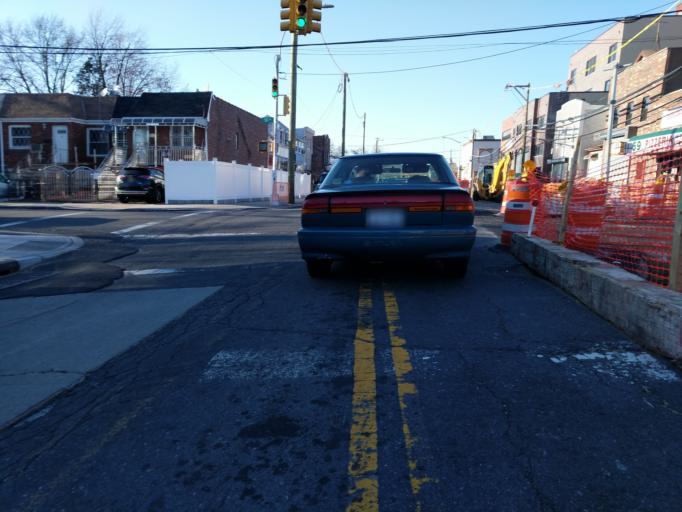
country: US
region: New York
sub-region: Queens County
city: Long Island City
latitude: 40.7368
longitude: -73.8960
